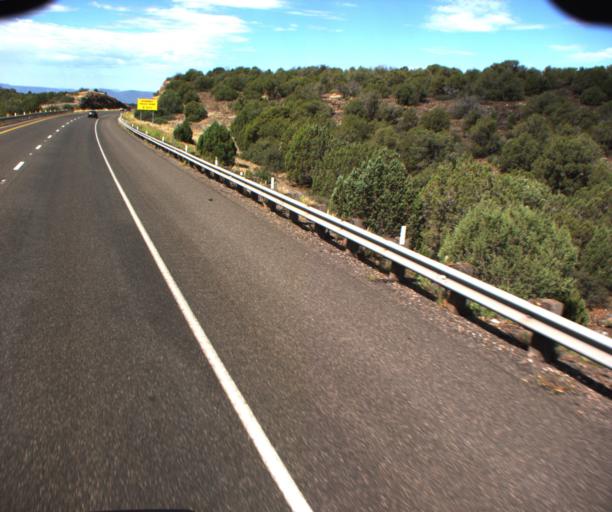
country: US
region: Arizona
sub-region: Yavapai County
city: Big Park
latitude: 34.7267
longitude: -111.7110
